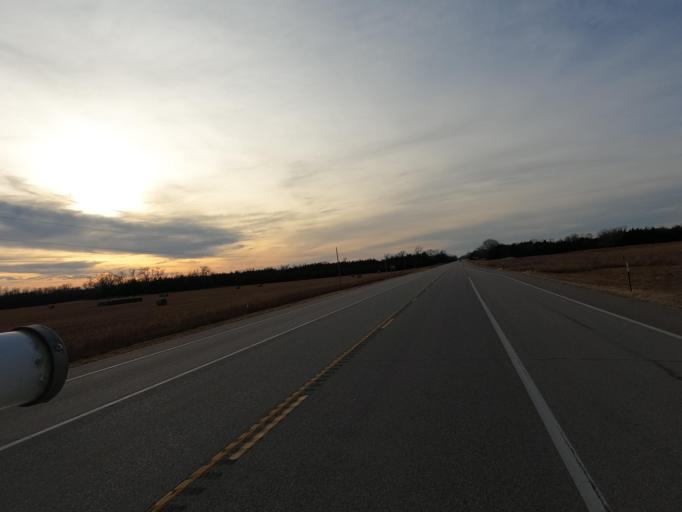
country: US
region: Kansas
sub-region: Rice County
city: Sterling
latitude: 37.9845
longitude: -98.2525
